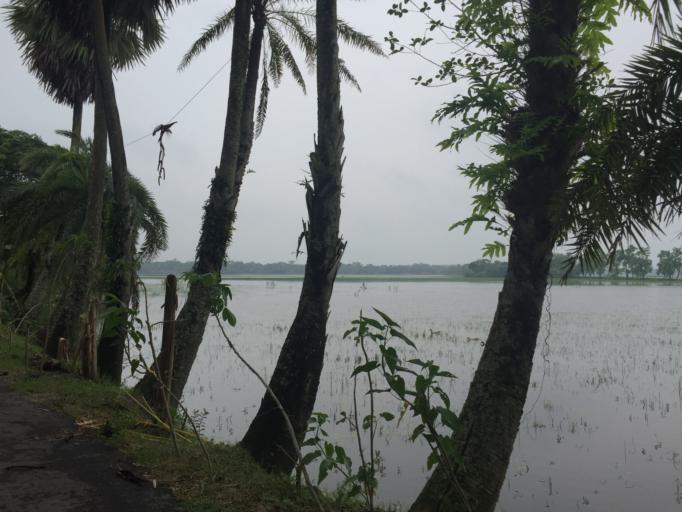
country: BD
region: Barisal
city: Mathba
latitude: 22.2122
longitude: 89.9229
